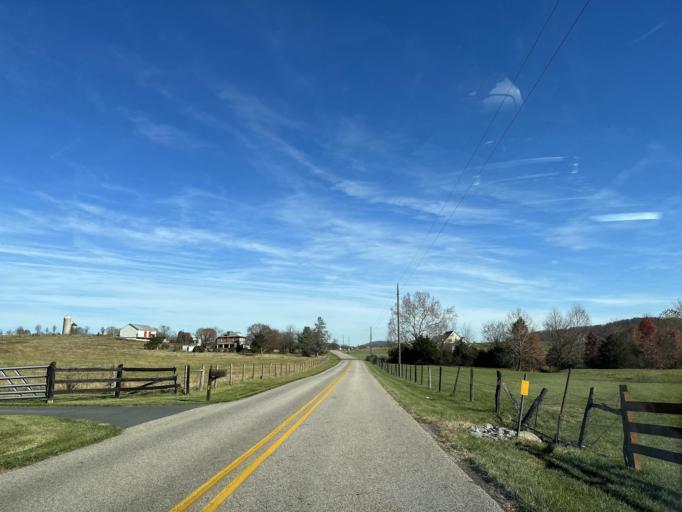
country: US
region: Virginia
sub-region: Augusta County
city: Fishersville
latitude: 38.1387
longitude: -78.9389
